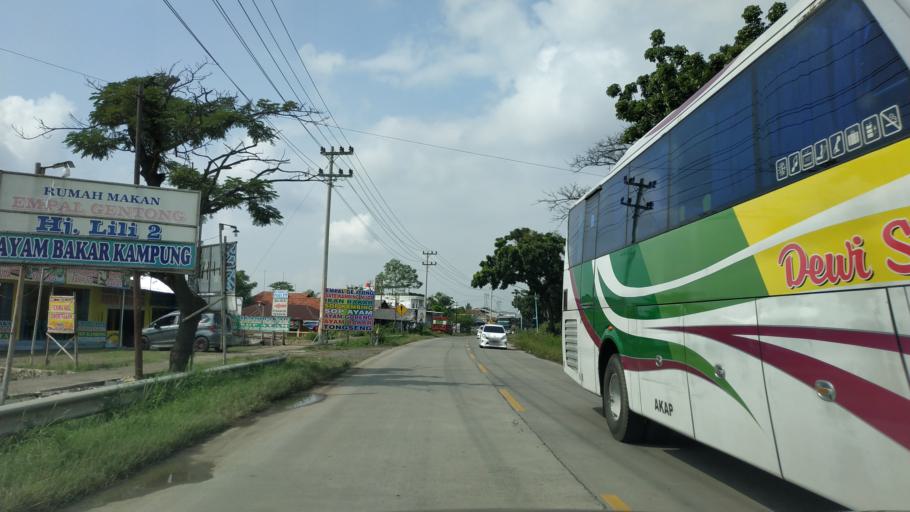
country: ID
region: Central Java
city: Ketanggungan
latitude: -6.9022
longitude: 108.8886
